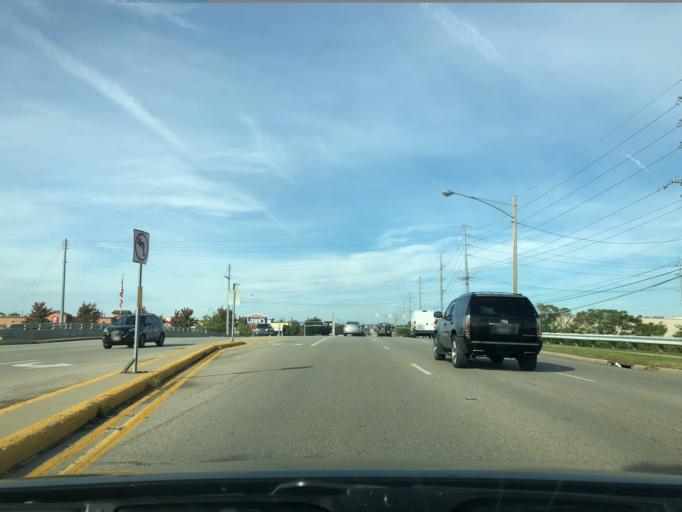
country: US
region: Ohio
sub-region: Hamilton County
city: Glendale
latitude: 39.2872
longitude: -84.4587
